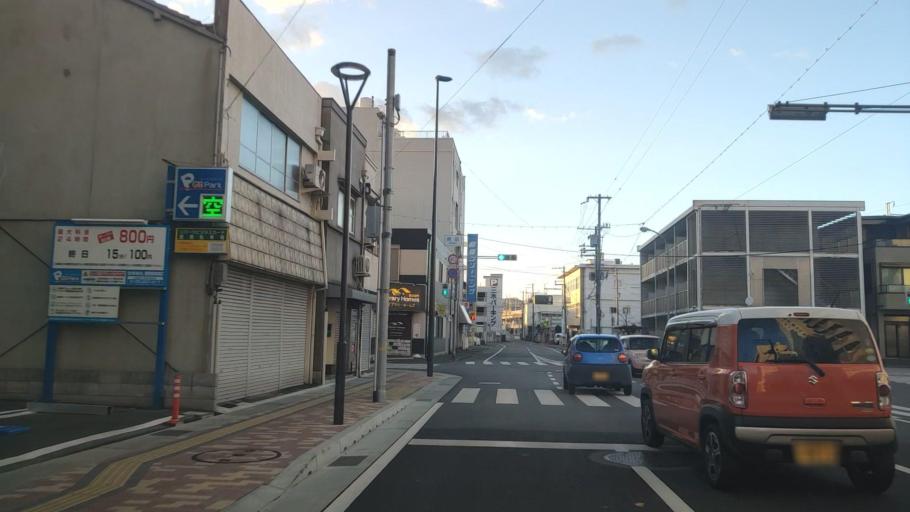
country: JP
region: Hyogo
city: Himeji
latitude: 34.8259
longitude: 134.6873
